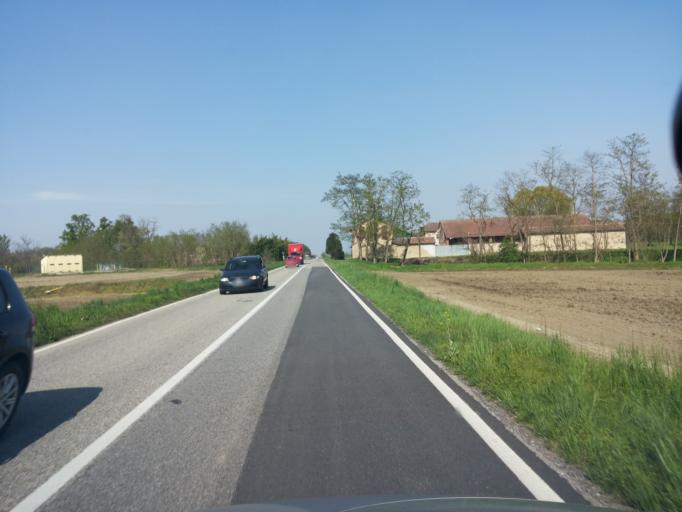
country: IT
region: Lombardy
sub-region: Provincia di Pavia
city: Zeme
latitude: 45.2100
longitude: 8.6465
